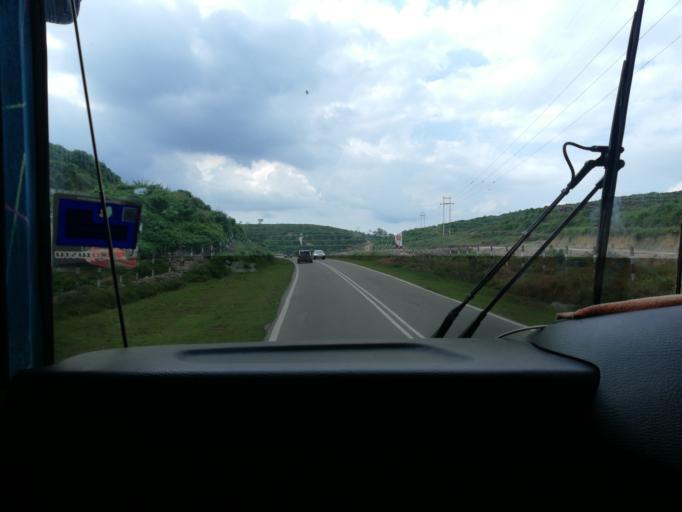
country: MY
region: Kedah
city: Kulim
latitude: 5.3067
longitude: 100.6144
